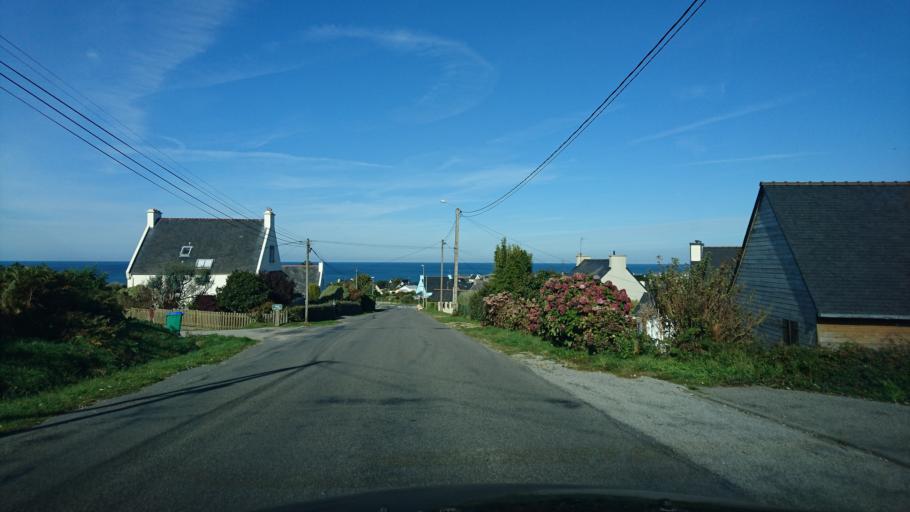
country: FR
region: Brittany
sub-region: Departement du Finistere
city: Lampaul-Plouarzel
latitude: 48.4351
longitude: -4.7733
